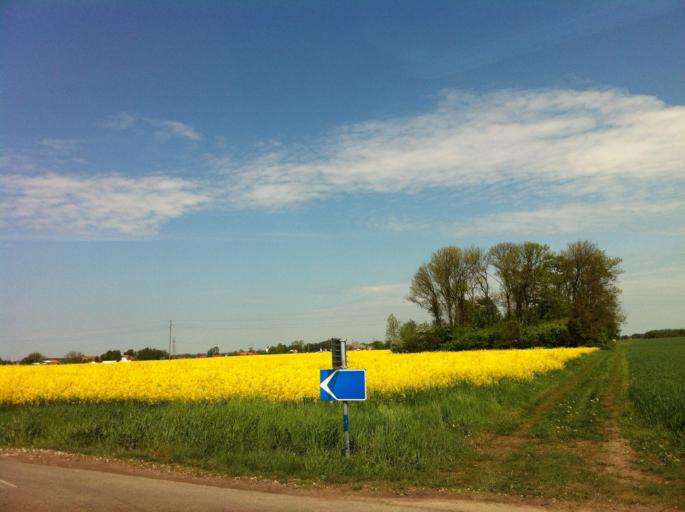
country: SE
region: Skane
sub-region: Helsingborg
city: Glumslov
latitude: 55.9188
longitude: 12.8678
